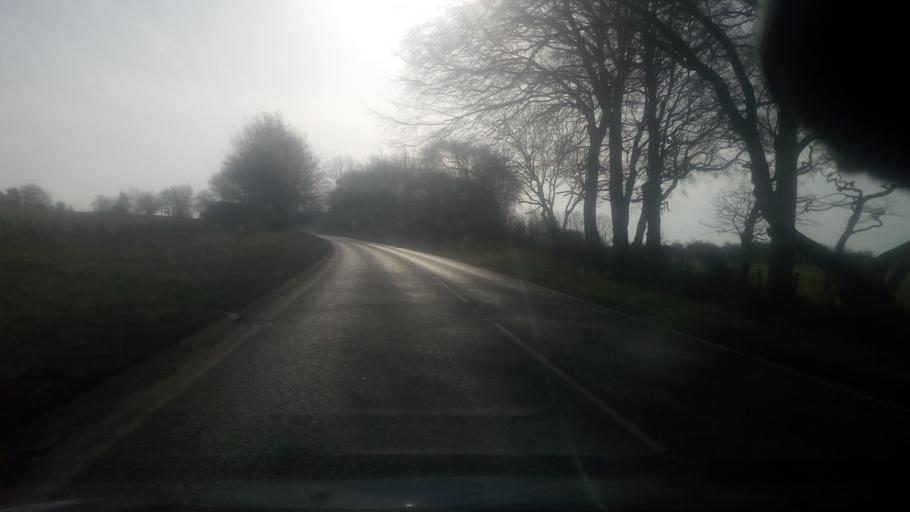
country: GB
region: England
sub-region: Northumberland
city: Corbridge
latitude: 55.0152
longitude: -2.0224
